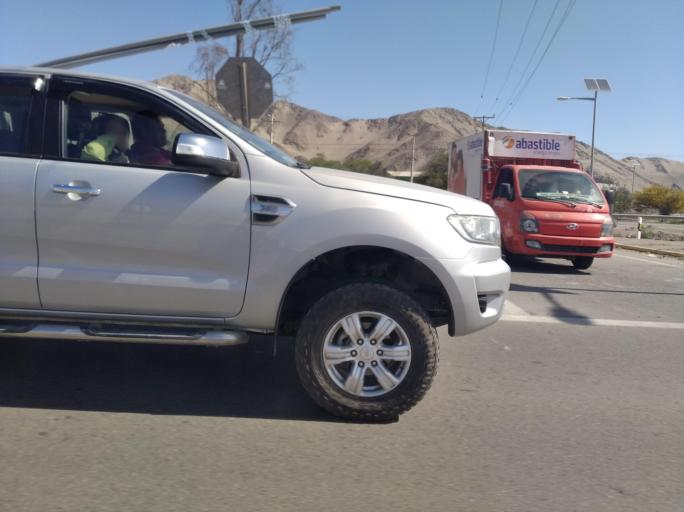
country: CL
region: Atacama
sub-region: Provincia de Copiapo
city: Copiapo
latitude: -27.3491
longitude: -70.3553
